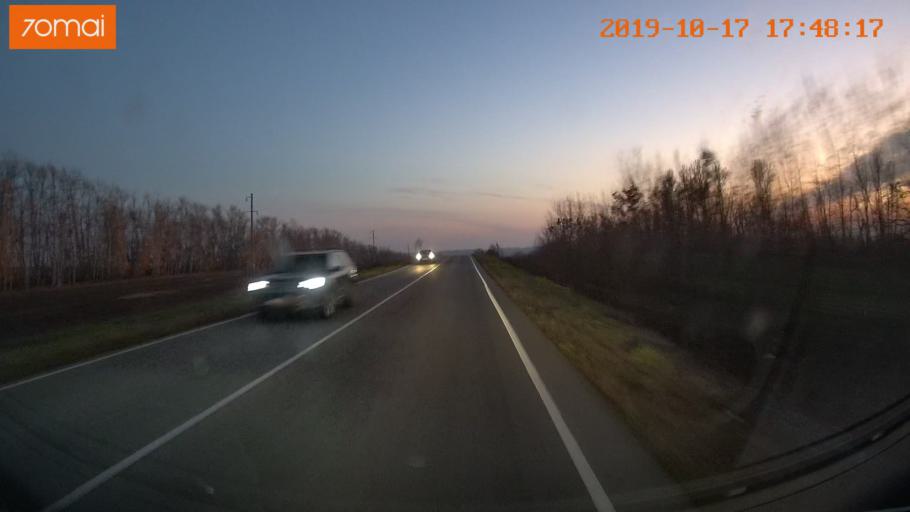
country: RU
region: Tula
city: Yepifan'
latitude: 53.6947
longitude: 38.6955
